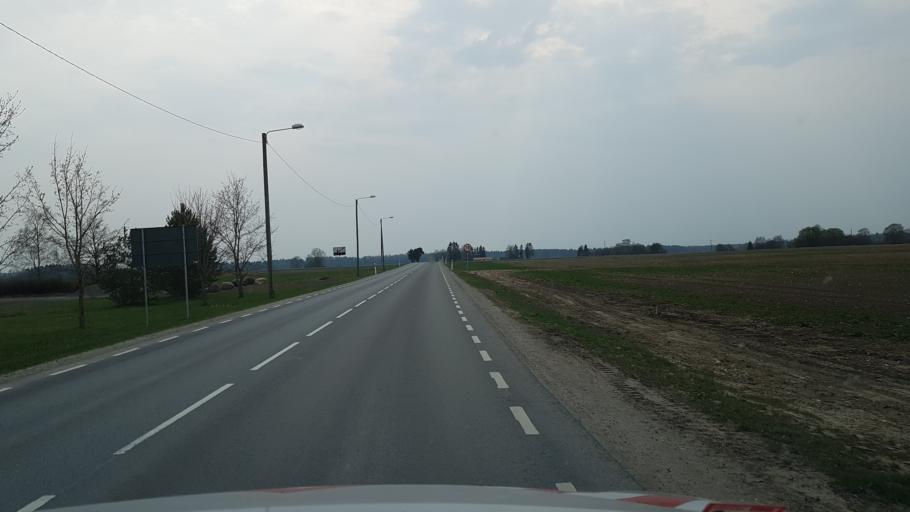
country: EE
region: Harju
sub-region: Anija vald
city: Kehra
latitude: 59.3325
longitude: 25.3273
